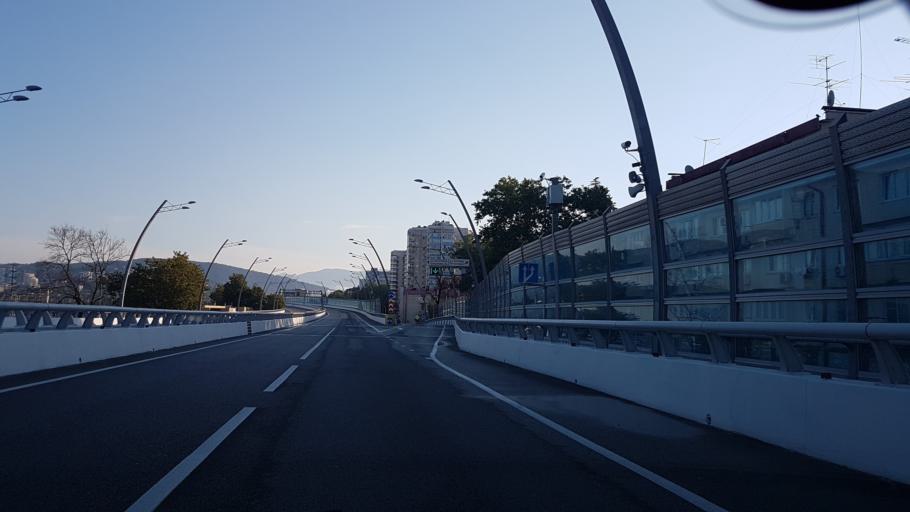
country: RU
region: Krasnodarskiy
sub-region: Sochi City
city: Sochi
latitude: 43.5928
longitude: 39.7308
